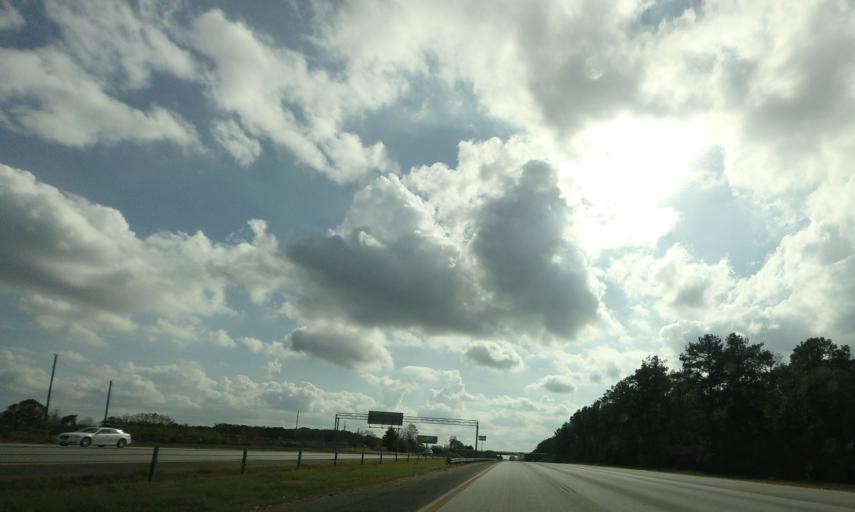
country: US
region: Georgia
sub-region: Houston County
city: Centerville
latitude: 32.5808
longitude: -83.7435
